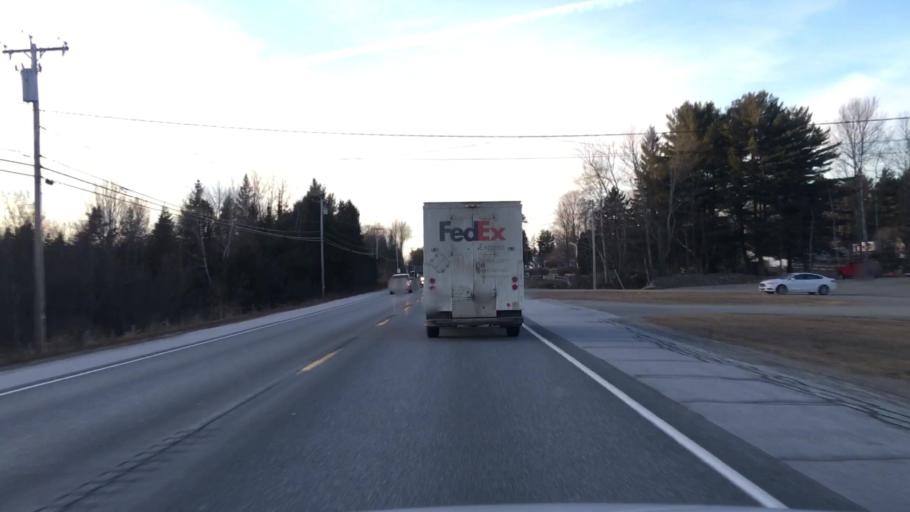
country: US
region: Maine
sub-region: Penobscot County
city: Holden
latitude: 44.7535
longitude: -68.6580
